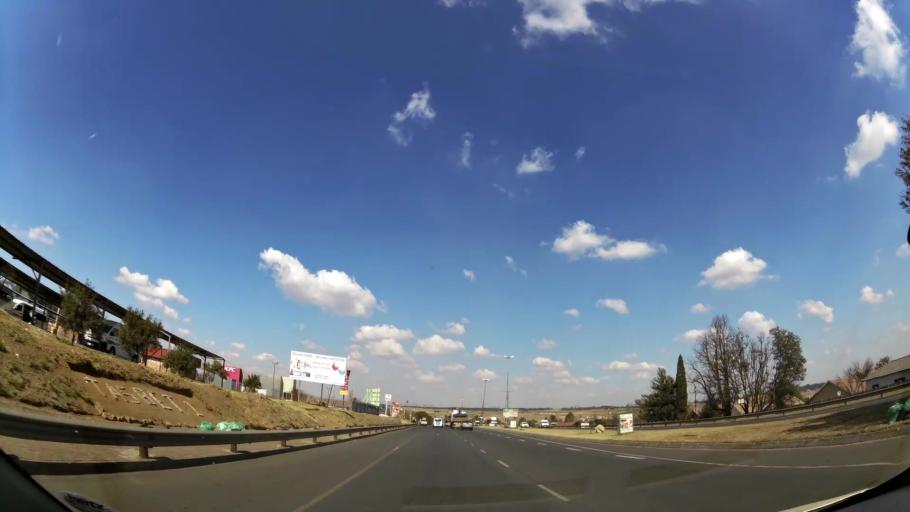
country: ZA
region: Mpumalanga
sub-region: Nkangala District Municipality
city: Witbank
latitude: -25.9248
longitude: 29.2347
